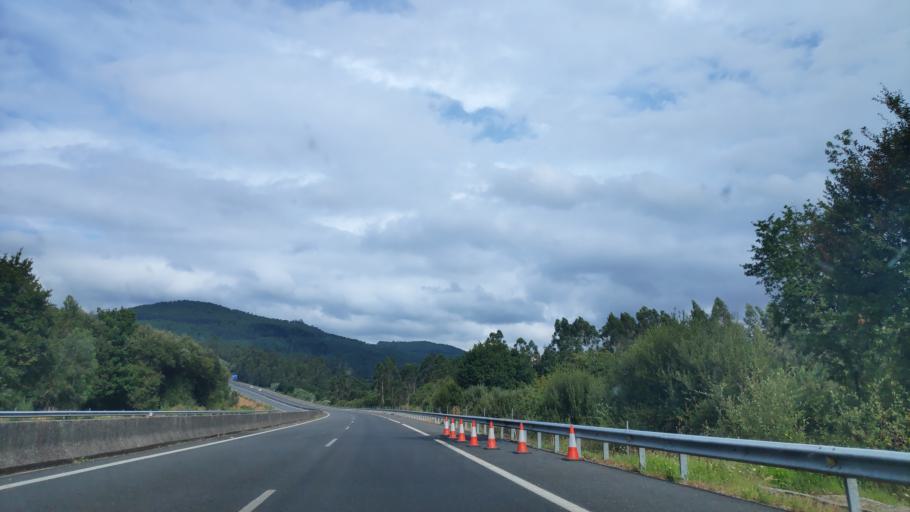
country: ES
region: Galicia
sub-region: Provincia da Coruna
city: Padron
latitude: 42.7294
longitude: -8.6857
